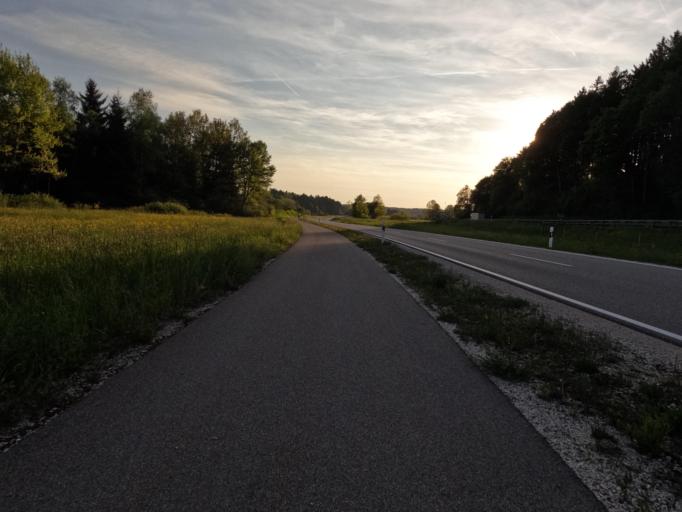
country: DE
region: Bavaria
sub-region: Upper Bavaria
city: Surberg
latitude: 47.8286
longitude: 12.7176
